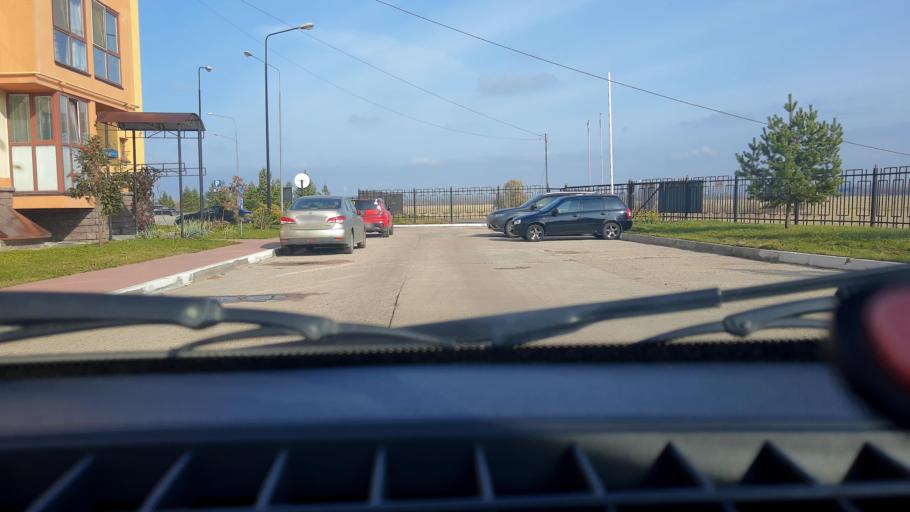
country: RU
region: Bashkortostan
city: Ufa
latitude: 54.7972
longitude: 55.9607
